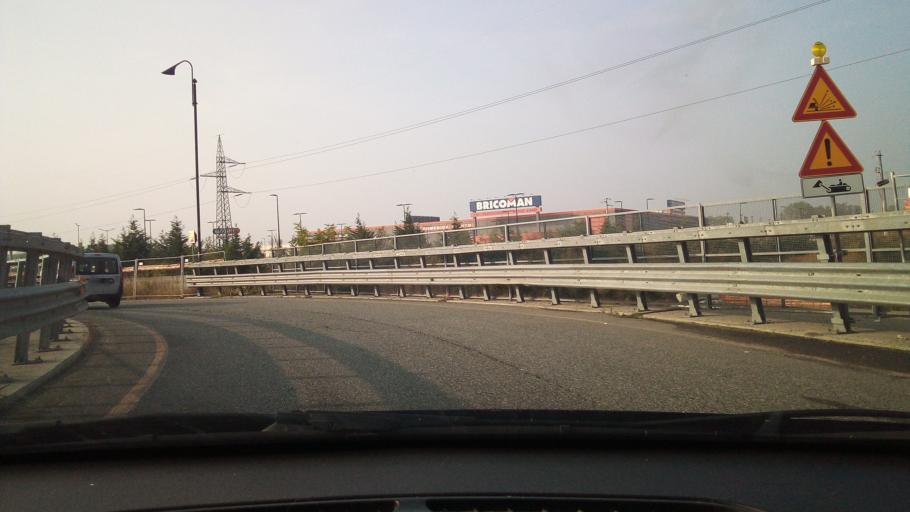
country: IT
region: Lombardy
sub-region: Citta metropolitana di Milano
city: Novegro-Tregarezzo-San Felice
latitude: 45.4876
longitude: 9.2639
